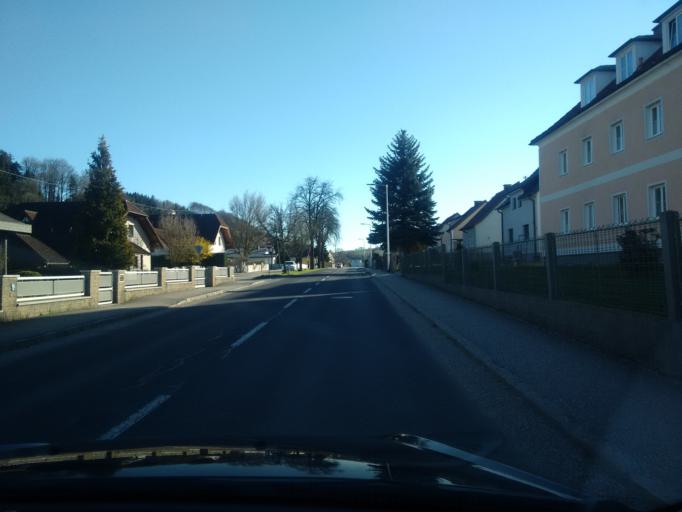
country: AT
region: Upper Austria
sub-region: Wels-Land
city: Offenhausen
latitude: 48.1543
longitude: 13.8357
